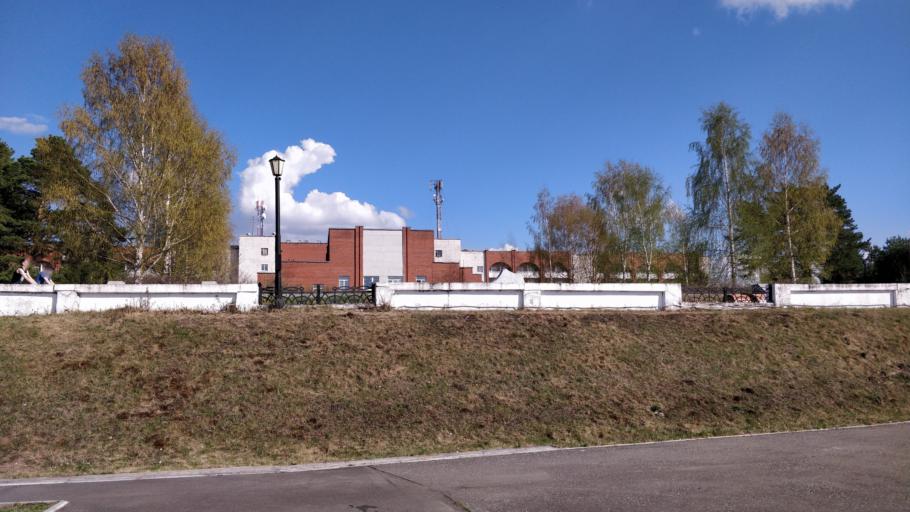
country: RU
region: Perm
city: Ust'-Kachka
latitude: 58.0072
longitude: 55.6653
